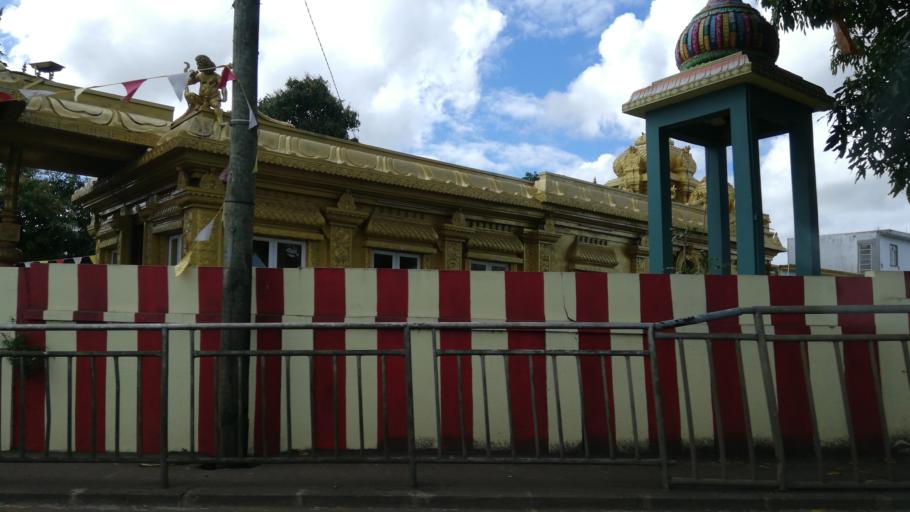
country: MU
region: Flacq
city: Lalmatie
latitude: -20.2104
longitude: 57.6773
